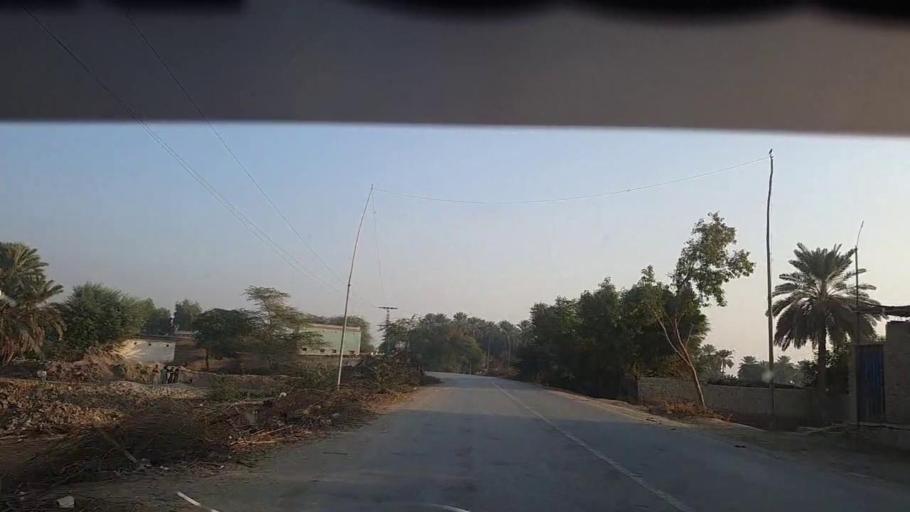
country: PK
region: Sindh
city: Ranipur
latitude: 27.2616
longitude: 68.5252
